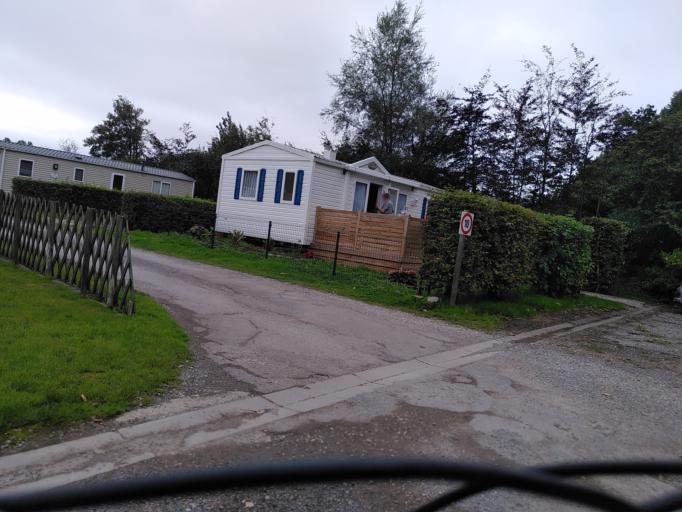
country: FR
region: Nord-Pas-de-Calais
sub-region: Departement du Pas-de-Calais
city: Mametz
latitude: 50.6421
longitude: 2.3003
